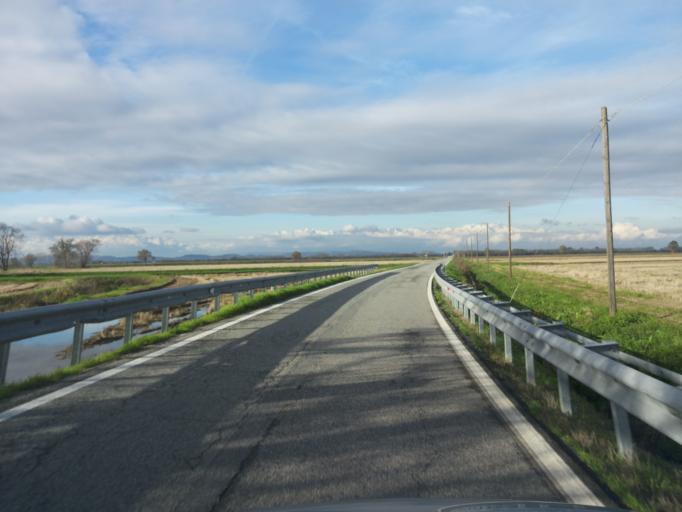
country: IT
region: Piedmont
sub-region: Provincia di Vercelli
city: Crova
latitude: 45.3098
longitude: 8.2023
